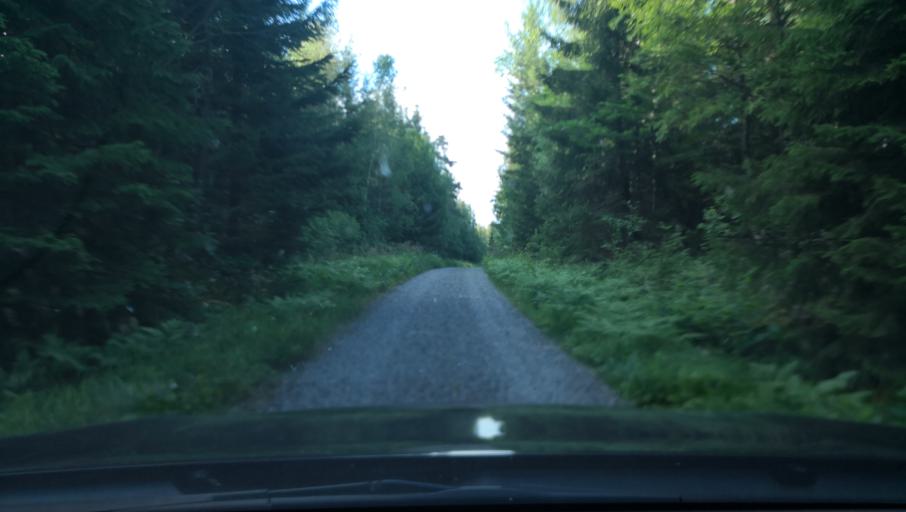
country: SE
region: Uppsala
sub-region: Osthammars Kommun
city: Osterbybruk
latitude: 60.0275
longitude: 17.9178
